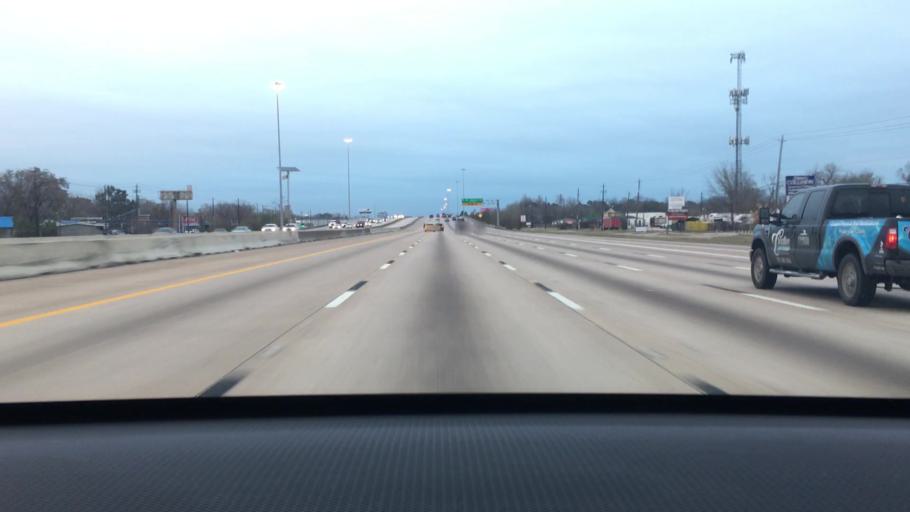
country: US
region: Texas
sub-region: Harris County
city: Aldine
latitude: 29.8743
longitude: -95.3276
